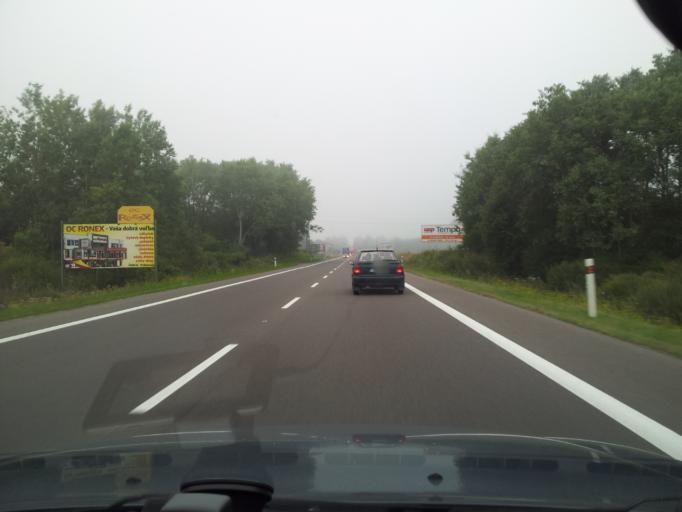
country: SK
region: Zilinsky
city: Cadca
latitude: 49.4109
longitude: 18.8414
